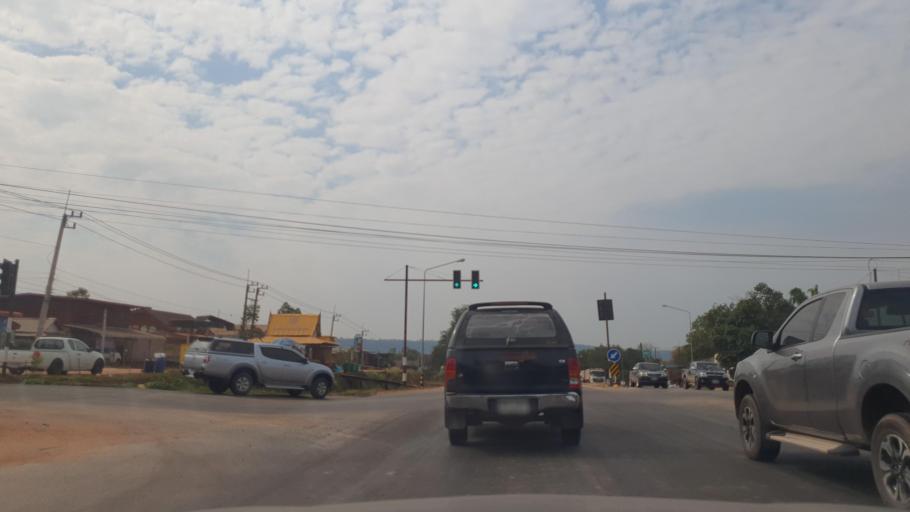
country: TH
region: Changwat Bueng Kan
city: Bung Khla
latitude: 18.2761
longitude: 103.8561
